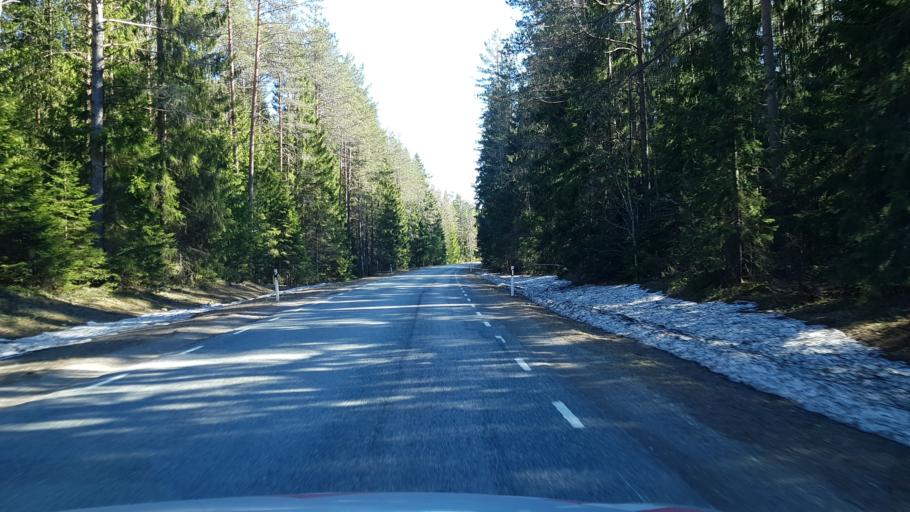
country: EE
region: Laeaene-Virumaa
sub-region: Vinni vald
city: Vinni
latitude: 59.2580
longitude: 26.6849
